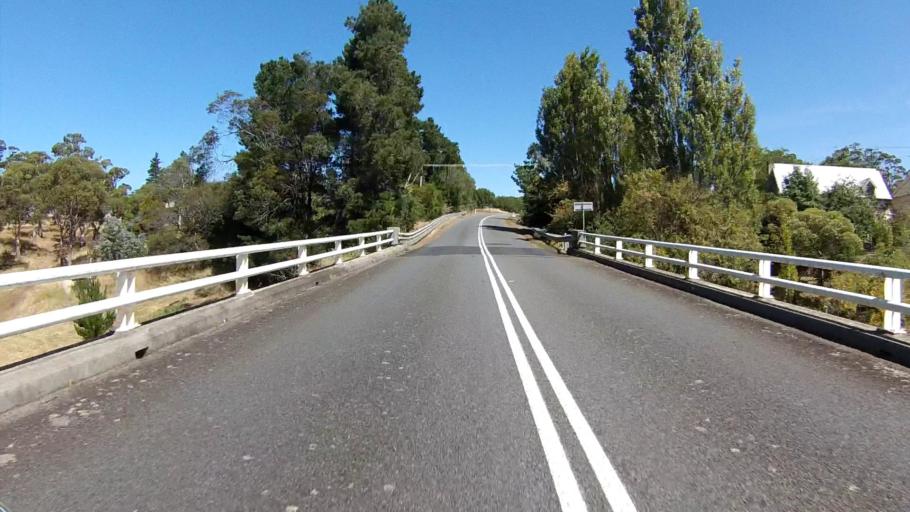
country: AU
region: Tasmania
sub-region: Sorell
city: Sorell
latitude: -42.2855
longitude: 147.9973
